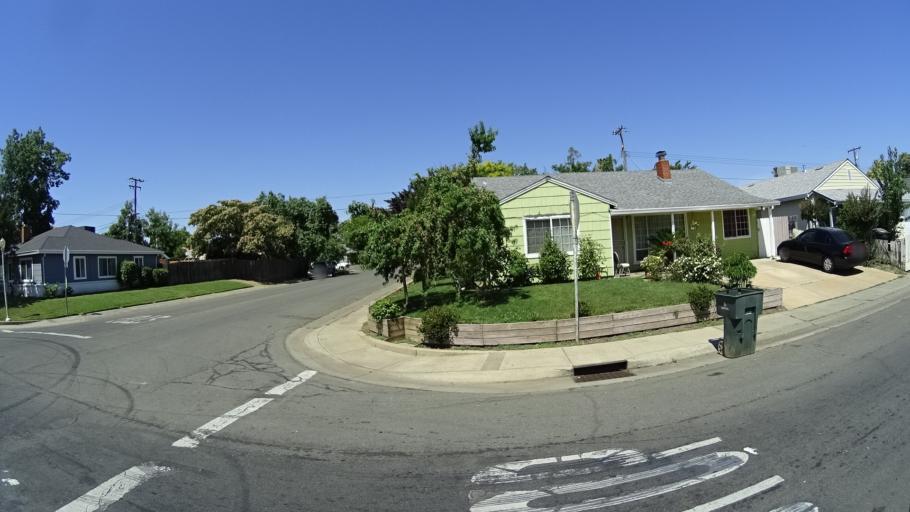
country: US
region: California
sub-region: Sacramento County
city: Florin
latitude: 38.5280
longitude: -121.4143
